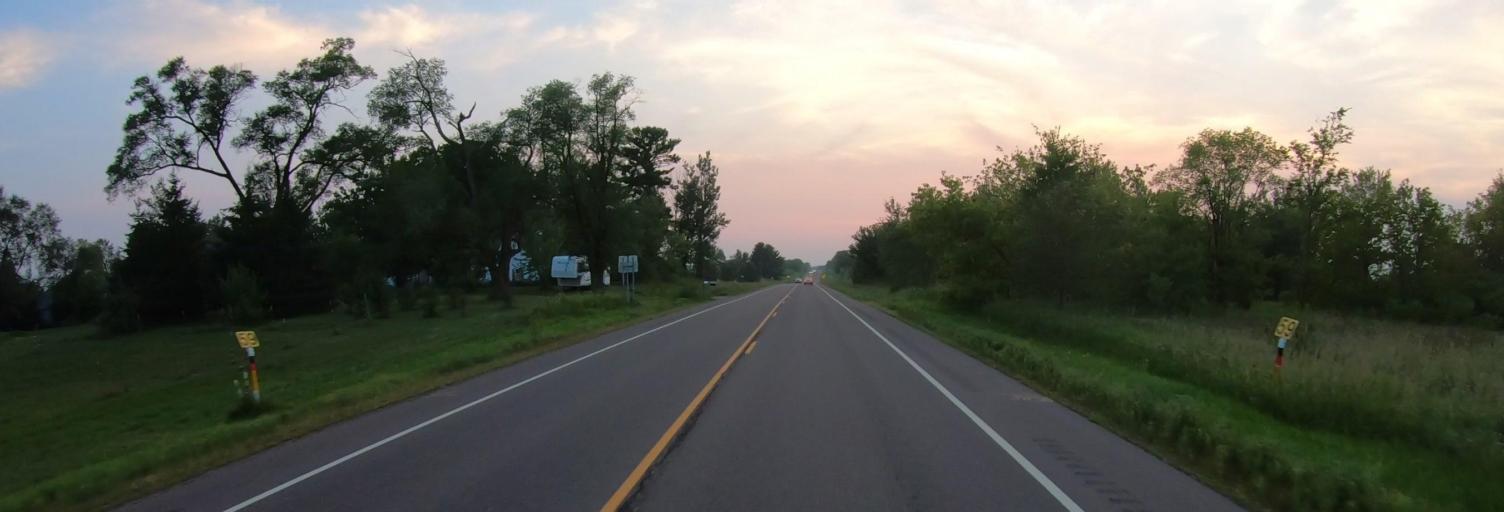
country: US
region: Minnesota
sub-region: Pine County
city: Rock Creek
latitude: 45.7734
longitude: -92.9355
